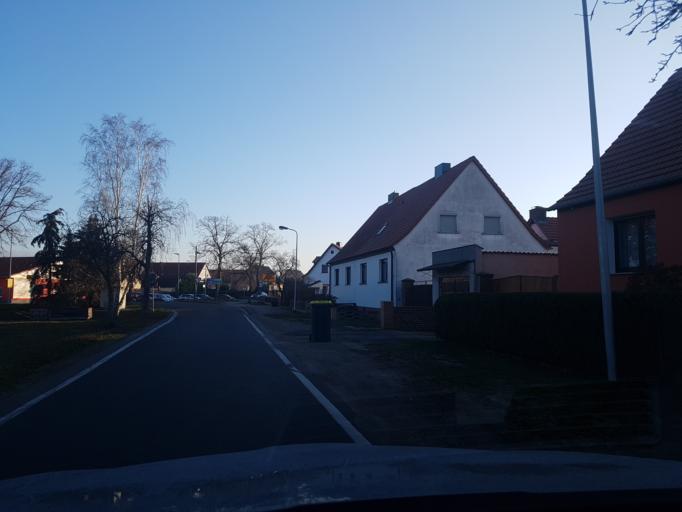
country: DE
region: Brandenburg
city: Schlieben
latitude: 51.7216
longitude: 13.3770
